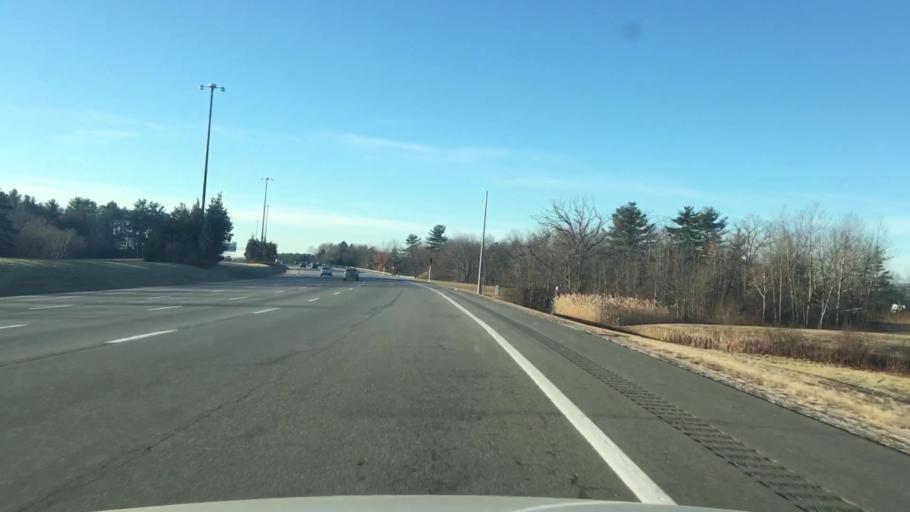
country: US
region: New Hampshire
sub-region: Rockingham County
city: Greenland
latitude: 43.0558
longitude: -70.8080
